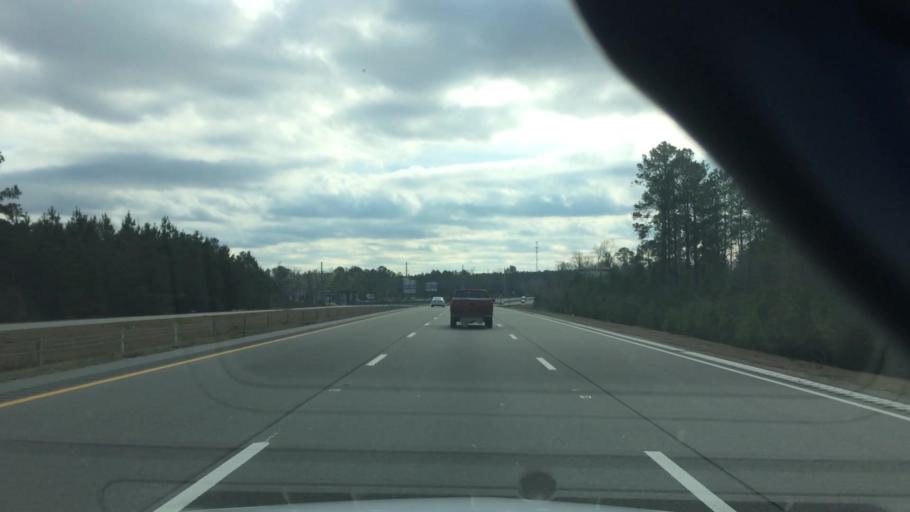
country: US
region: North Carolina
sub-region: Brunswick County
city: Leland
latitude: 34.1857
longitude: -78.0823
